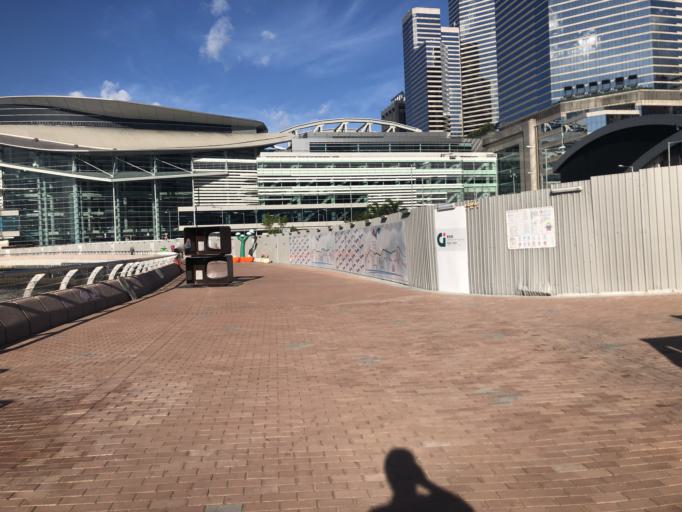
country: HK
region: Wanchai
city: Wan Chai
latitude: 22.2826
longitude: 114.1701
